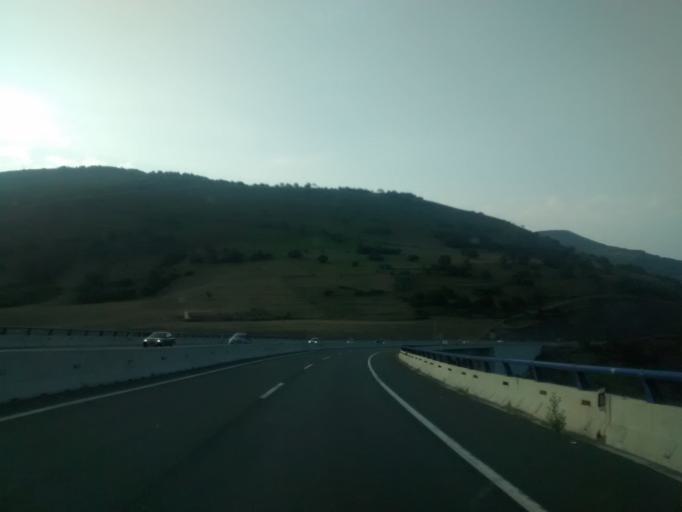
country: ES
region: Cantabria
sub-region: Provincia de Cantabria
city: Pesquera
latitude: 43.1033
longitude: -4.0900
